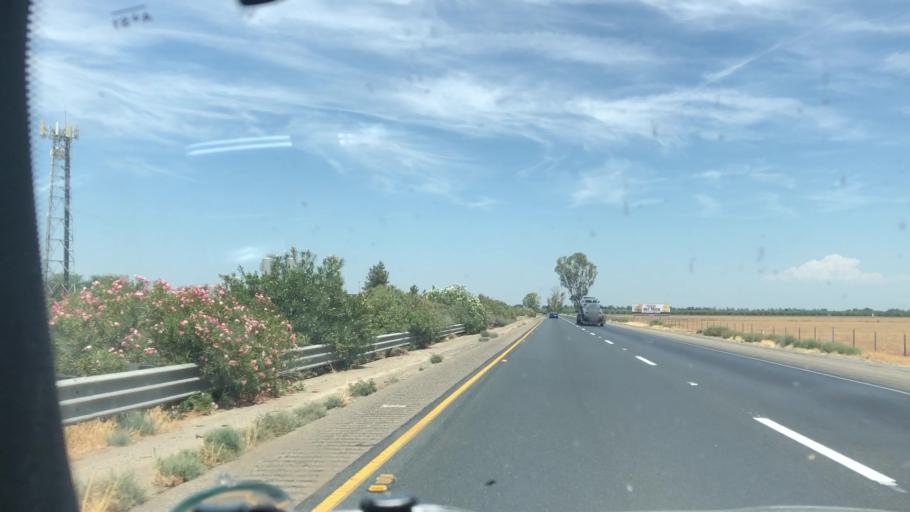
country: US
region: California
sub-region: Tulare County
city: Tipton
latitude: 36.1286
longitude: -119.3252
